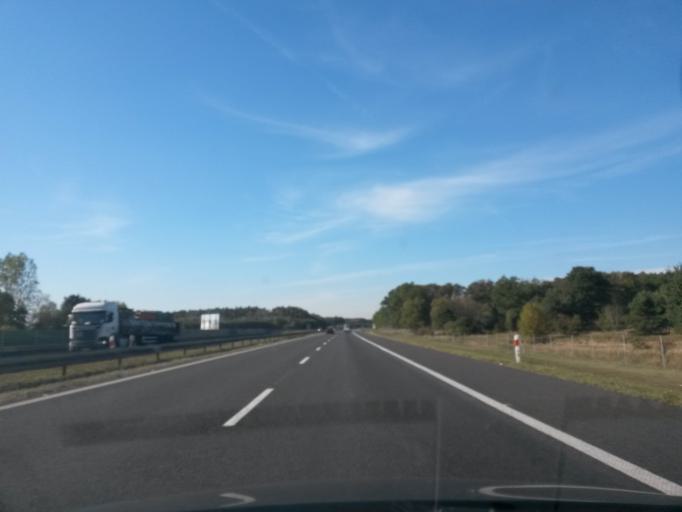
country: PL
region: Opole Voivodeship
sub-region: Powiat opolski
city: Niemodlin
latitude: 50.6808
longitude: 17.6469
